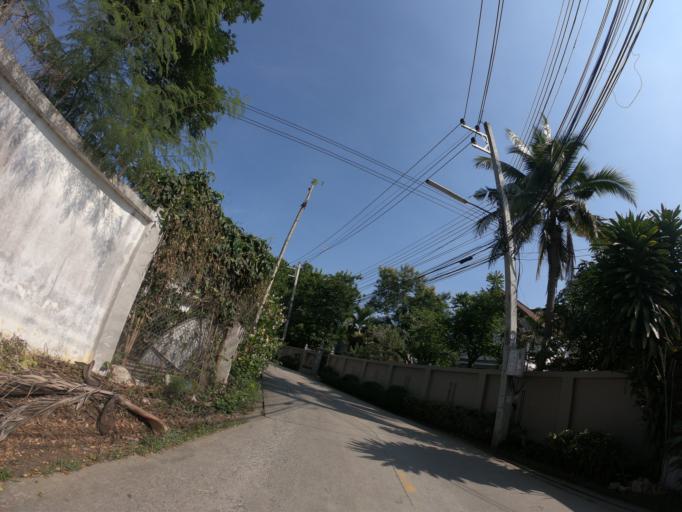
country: TH
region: Chiang Mai
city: Chiang Mai
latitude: 18.7767
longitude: 99.0223
